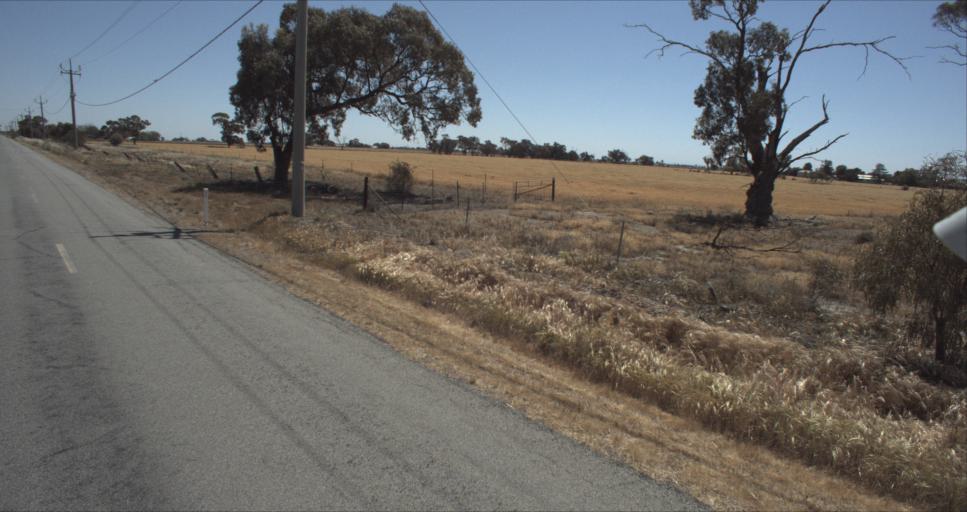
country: AU
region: New South Wales
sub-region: Leeton
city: Leeton
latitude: -34.5190
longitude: 146.4129
